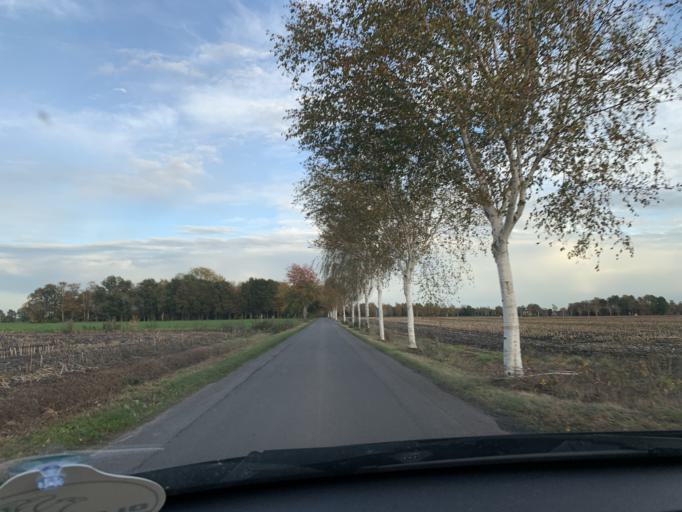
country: DE
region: Lower Saxony
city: Wiefelstede
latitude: 53.2525
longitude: 8.0840
